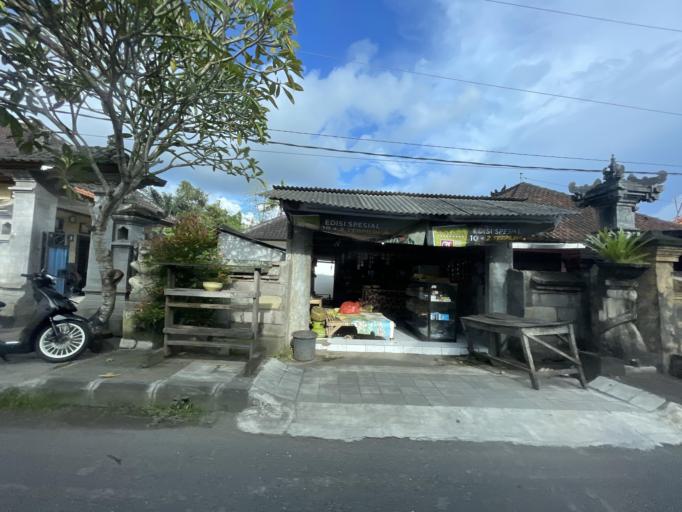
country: ID
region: Bali
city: Banjar Desa
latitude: -8.5753
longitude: 115.2867
